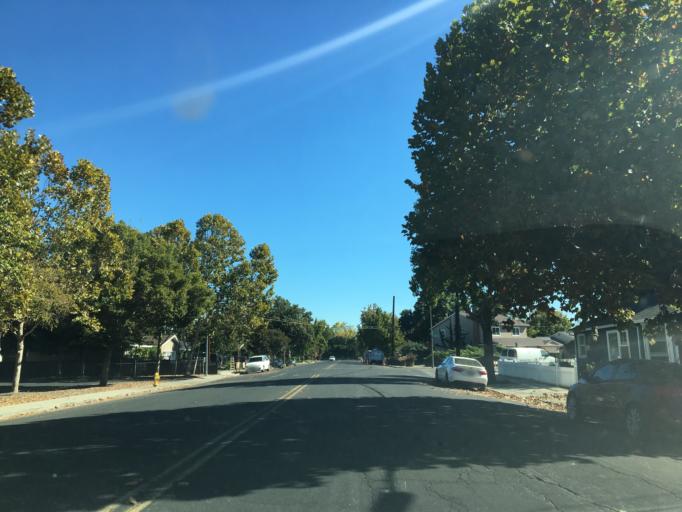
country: US
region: California
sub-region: Santa Clara County
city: Buena Vista
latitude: 37.3018
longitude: -121.8853
